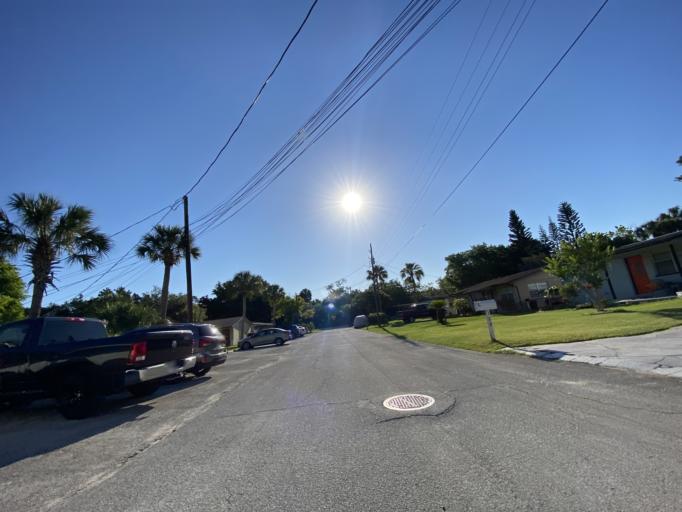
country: US
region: Florida
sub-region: Volusia County
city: Port Orange
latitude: 29.1481
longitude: -80.9927
